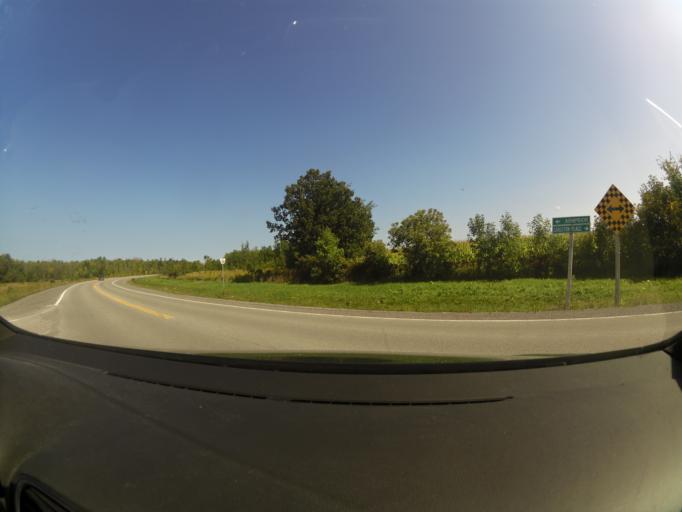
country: CA
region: Ontario
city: Arnprior
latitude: 45.4121
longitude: -76.3338
